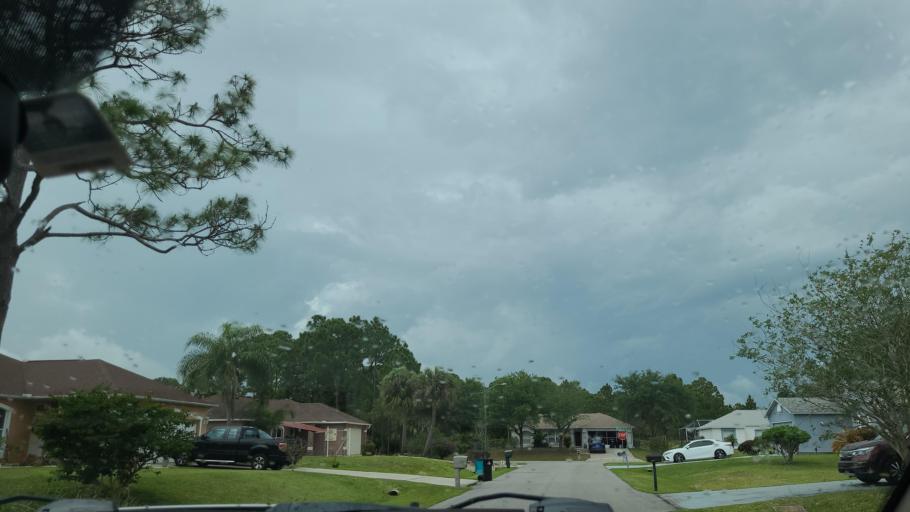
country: US
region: Florida
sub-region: Brevard County
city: Grant-Valkaria
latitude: 27.9452
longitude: -80.6382
